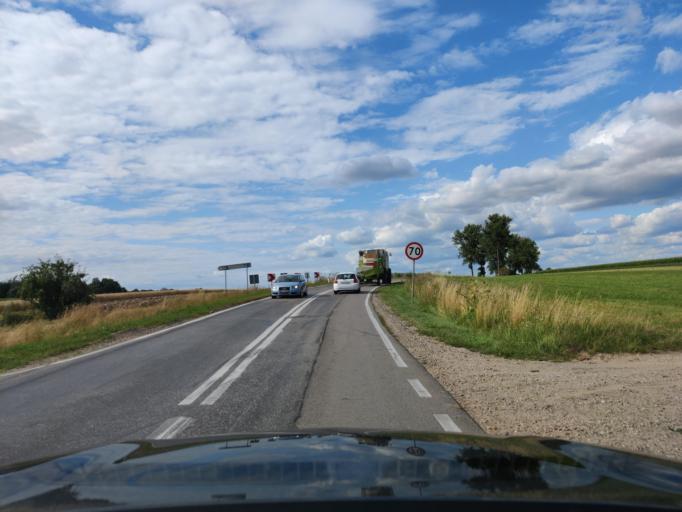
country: PL
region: Podlasie
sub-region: Powiat zambrowski
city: Zambrow
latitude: 52.8896
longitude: 22.2509
